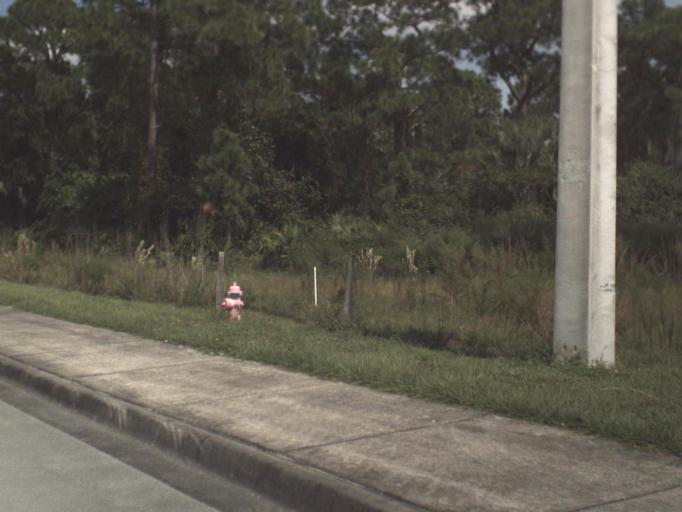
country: US
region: Florida
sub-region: Okeechobee County
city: Cypress Quarters
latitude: 27.2734
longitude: -80.8296
